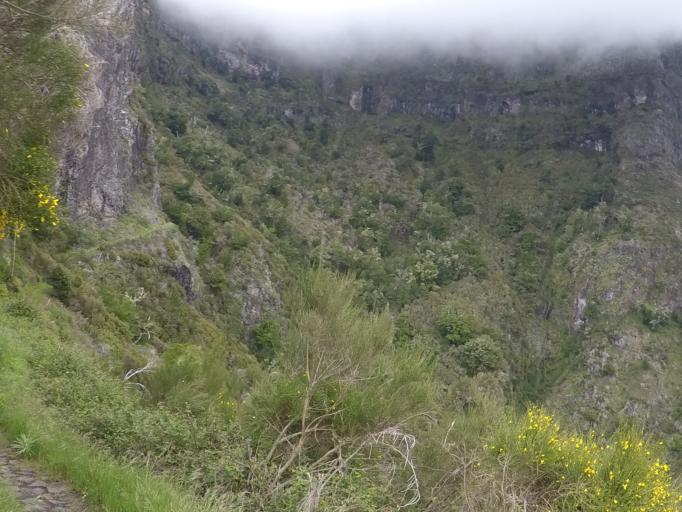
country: PT
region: Madeira
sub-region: Camara de Lobos
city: Curral das Freiras
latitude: 32.7335
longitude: -16.9984
